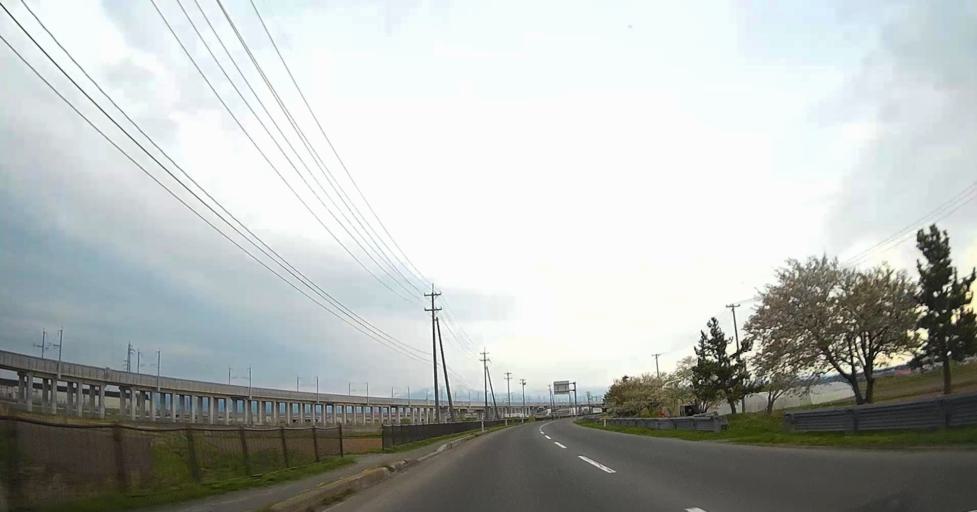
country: JP
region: Aomori
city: Aomori Shi
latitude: 40.8419
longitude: 140.6894
